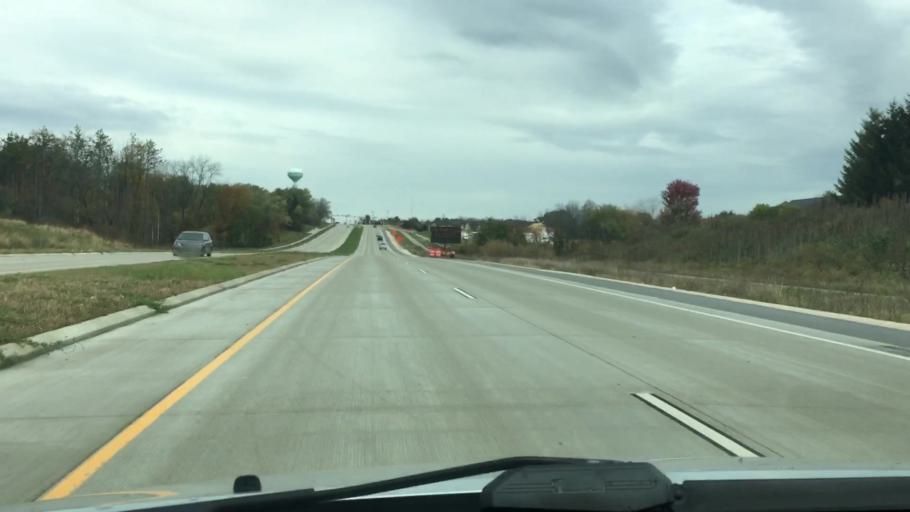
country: US
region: Wisconsin
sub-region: Waukesha County
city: Pewaukee
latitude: 43.0298
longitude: -88.2857
